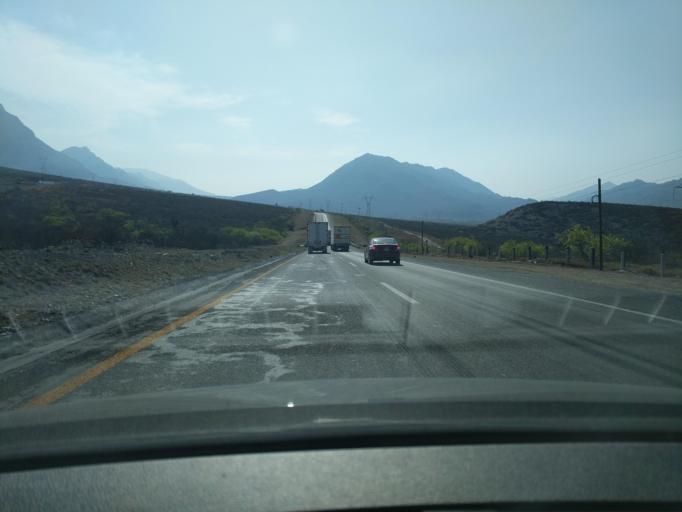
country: MX
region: Nuevo Leon
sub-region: Garcia
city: Las Torres de Guadalupe
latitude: 25.6740
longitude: -100.6867
